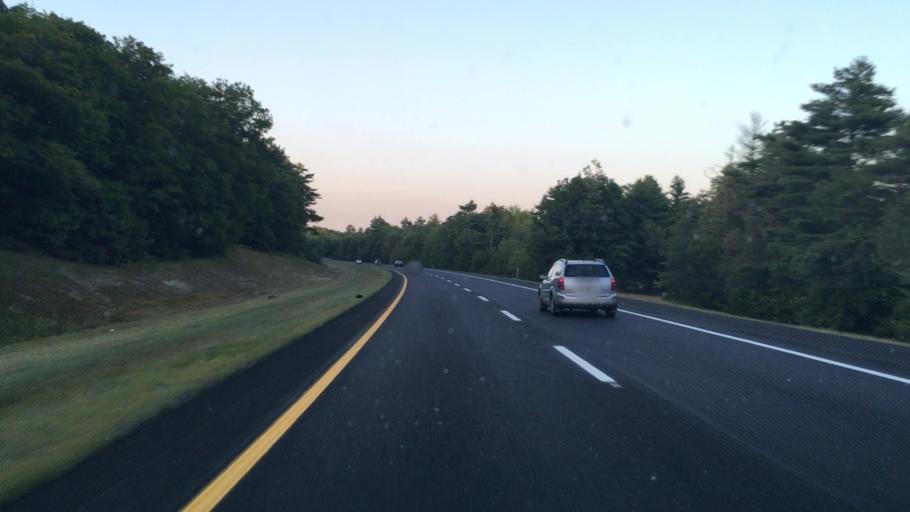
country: US
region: Maine
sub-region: Sagadahoc County
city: Topsham
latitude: 44.0040
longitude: -69.9257
